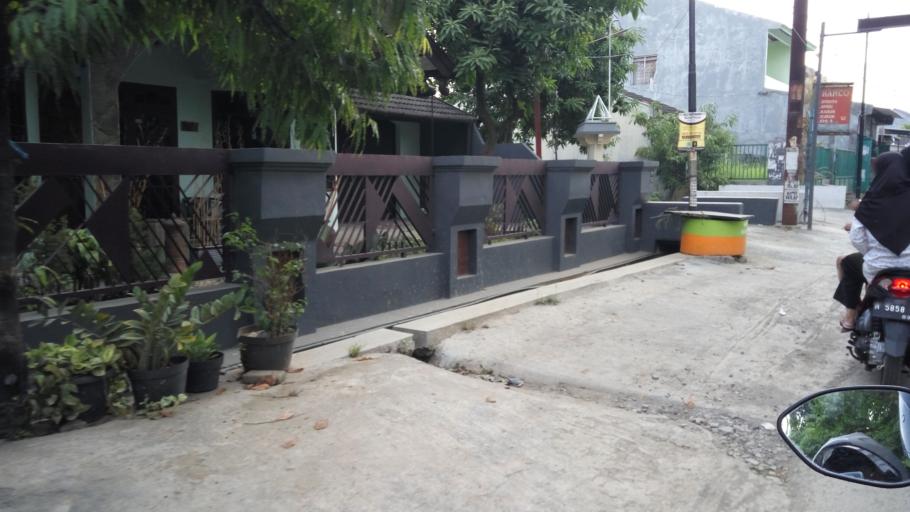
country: ID
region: Central Java
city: Mranggen
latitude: -7.0359
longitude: 110.4709
